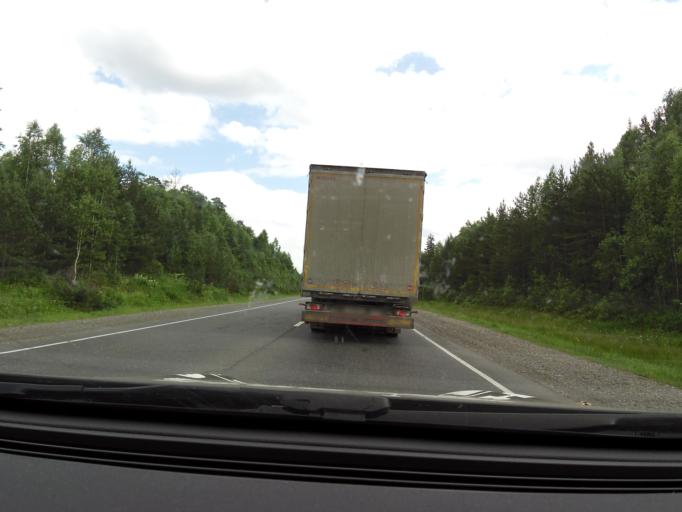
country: RU
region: Sverdlovsk
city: Atig
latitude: 56.7995
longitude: 59.3866
